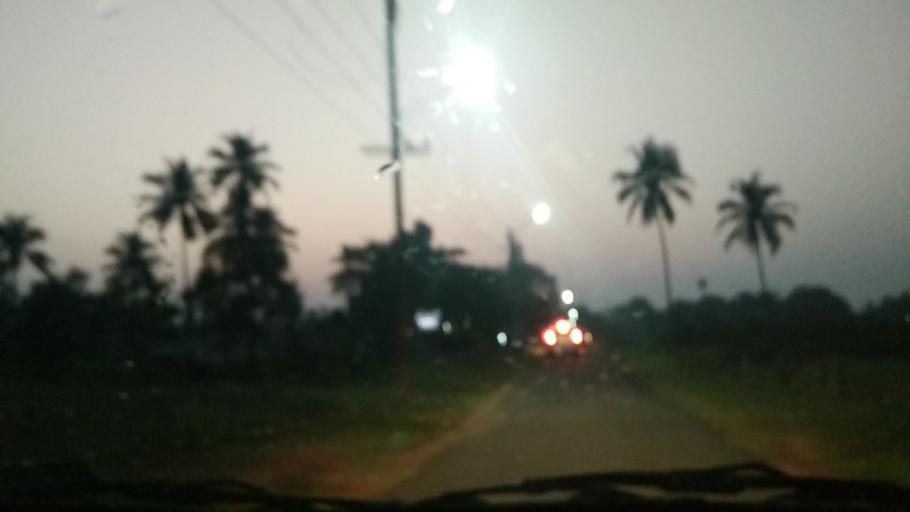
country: IN
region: Goa
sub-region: South Goa
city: Varca
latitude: 15.2057
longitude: 73.9434
